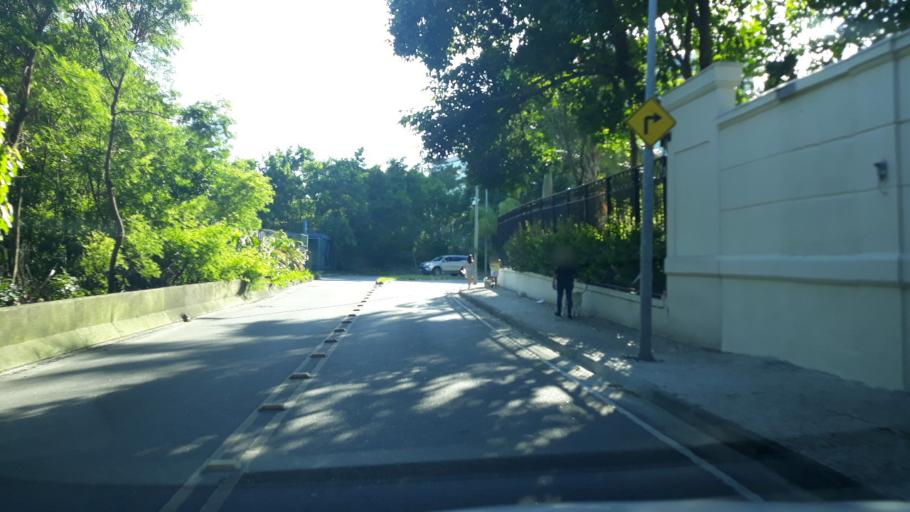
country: BR
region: Rio de Janeiro
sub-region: Rio De Janeiro
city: Rio de Janeiro
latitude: -22.9965
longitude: -43.3477
